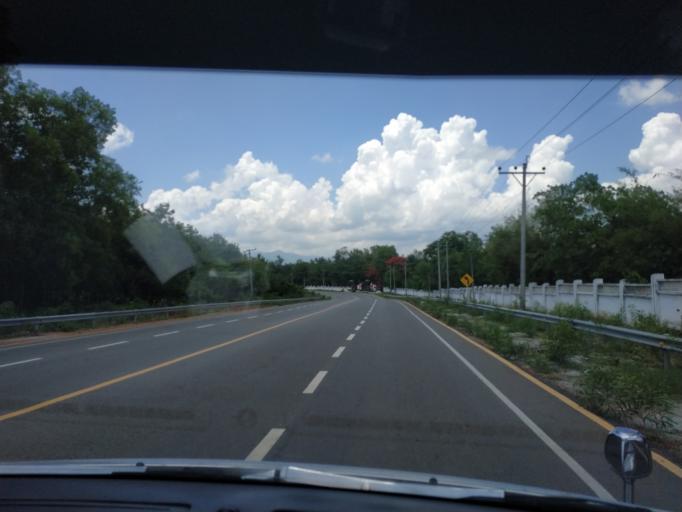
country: MM
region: Mon
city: Kyaikto
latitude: 17.3355
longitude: 97.0390
